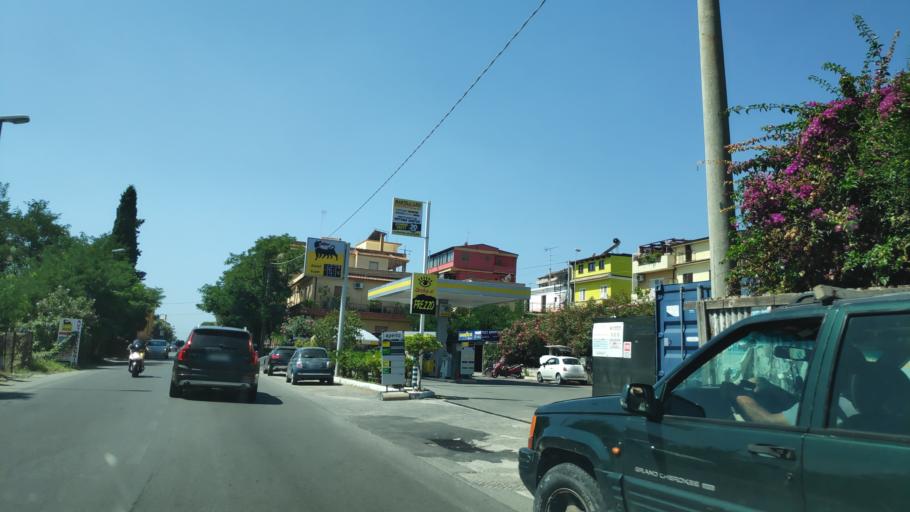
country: IT
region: Calabria
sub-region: Provincia di Reggio Calabria
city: Brancaleone
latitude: 37.9623
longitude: 16.1003
